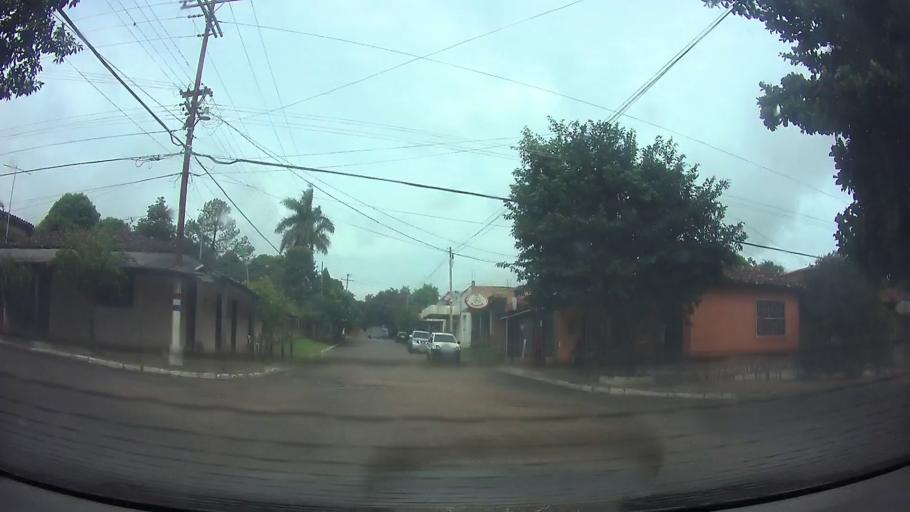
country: PY
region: Cordillera
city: Atyra
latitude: -25.2811
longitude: -57.1725
